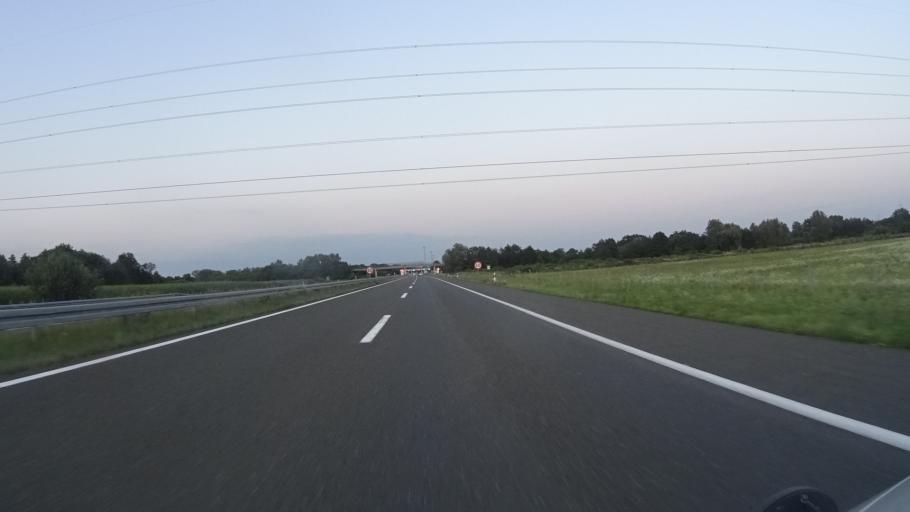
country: HR
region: Medimurska
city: Hodosan
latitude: 46.4129
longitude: 16.6325
